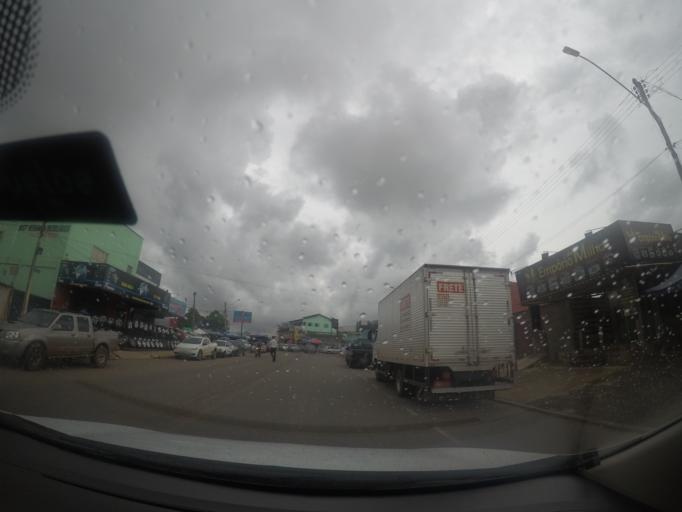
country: BR
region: Goias
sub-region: Trindade
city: Trindade
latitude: -16.6430
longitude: -49.3906
